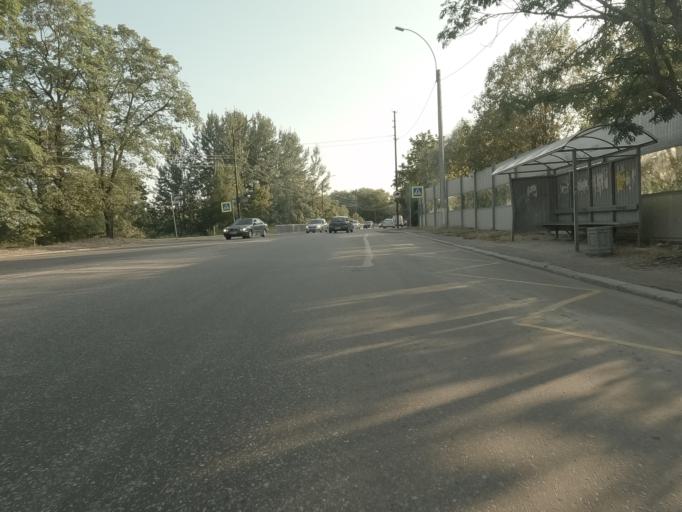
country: RU
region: Leningrad
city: Vyborg
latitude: 60.7210
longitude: 28.7673
